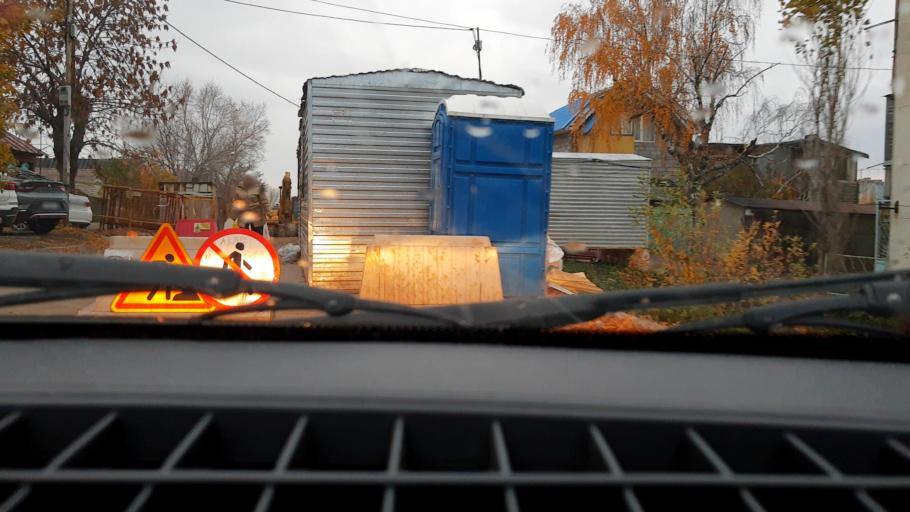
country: RU
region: Bashkortostan
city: Ufa
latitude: 54.7432
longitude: 55.9470
